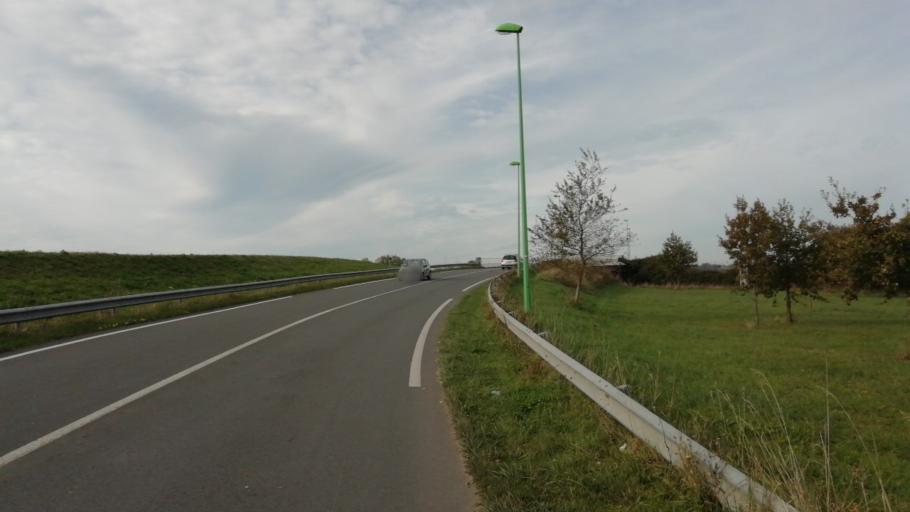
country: FR
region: Haute-Normandie
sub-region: Departement de la Seine-Maritime
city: Saint-Martin-du-Manoir
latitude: 49.5405
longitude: 0.2175
